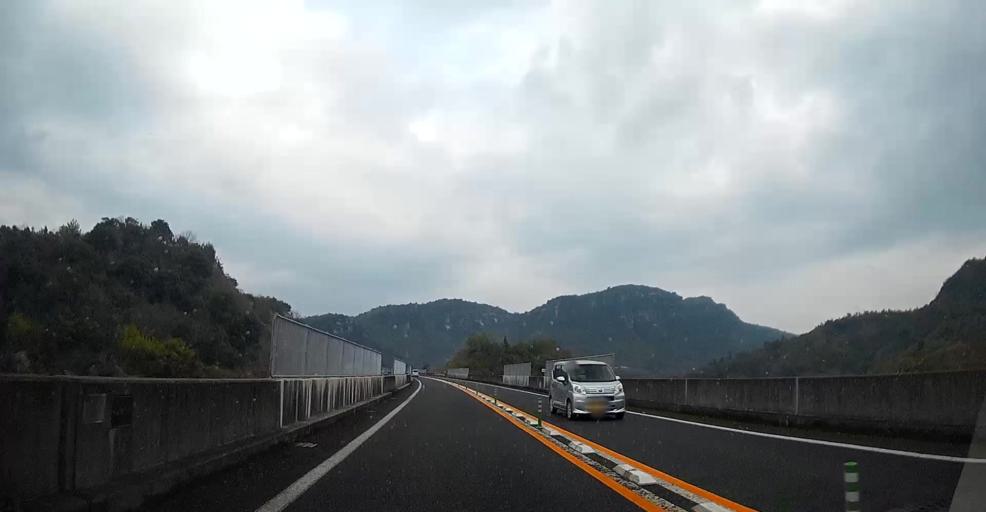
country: JP
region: Kumamoto
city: Hondo
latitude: 32.4990
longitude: 130.3970
